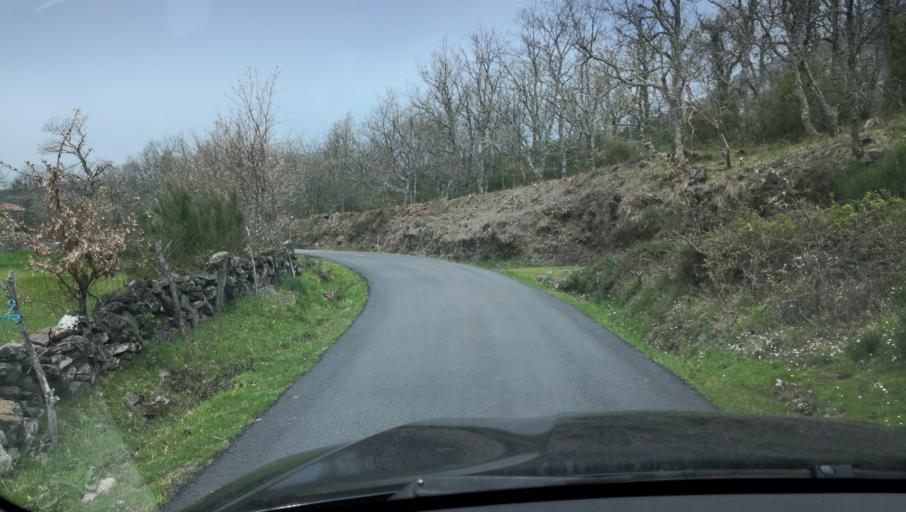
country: PT
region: Vila Real
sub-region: Vila Real
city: Vila Real
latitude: 41.2951
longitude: -7.8223
